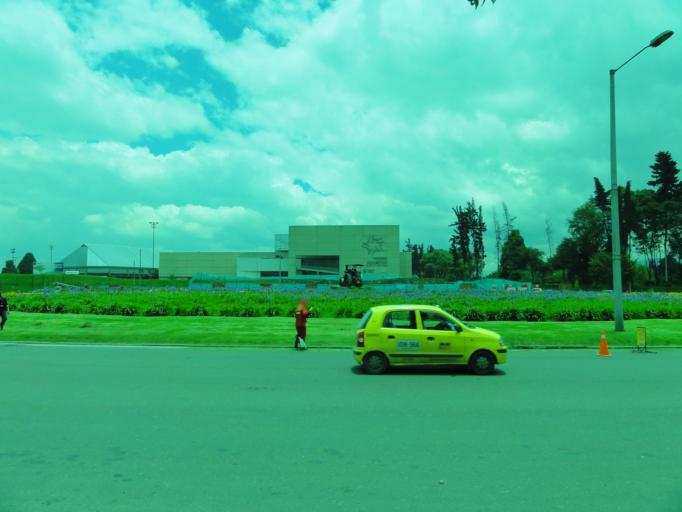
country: CO
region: Bogota D.C.
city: Bogota
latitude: 4.6529
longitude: -74.0839
